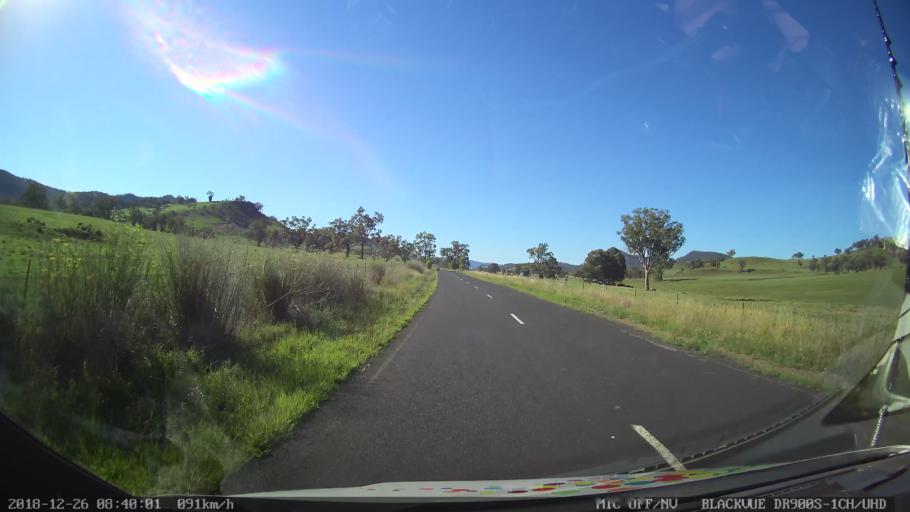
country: AU
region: New South Wales
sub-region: Mid-Western Regional
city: Kandos
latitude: -32.4613
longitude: 150.0757
